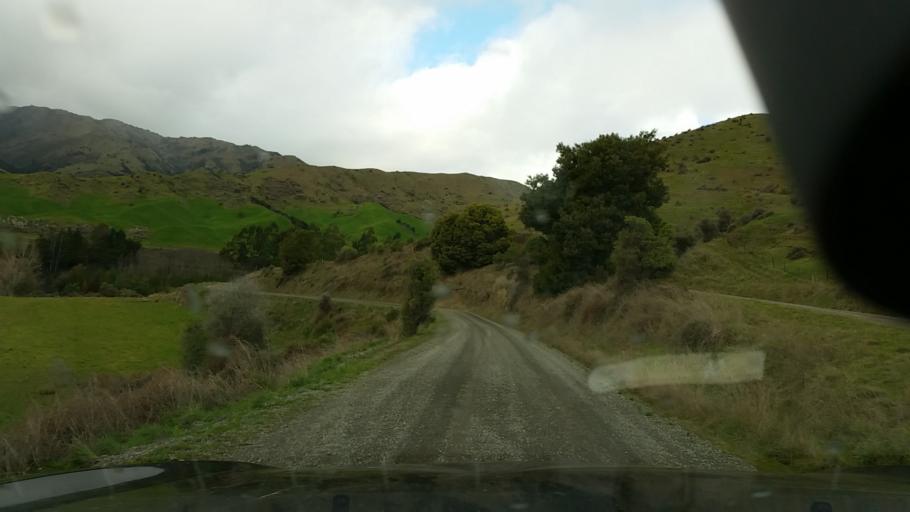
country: NZ
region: Marlborough
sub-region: Marlborough District
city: Blenheim
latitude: -41.6568
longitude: 173.6533
